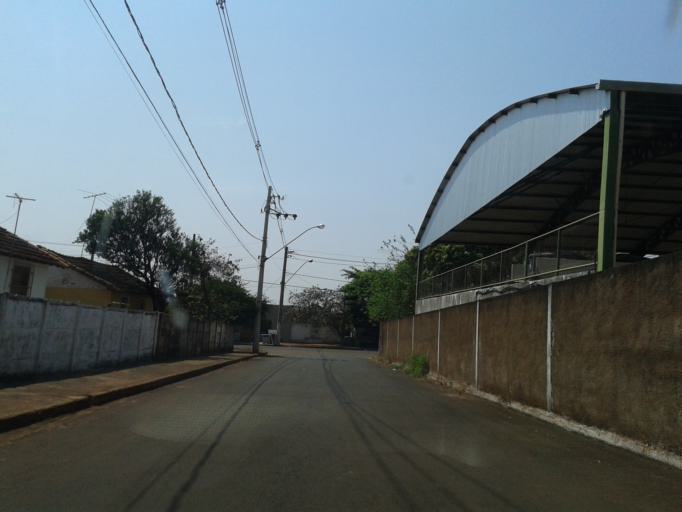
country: BR
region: Minas Gerais
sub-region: Ituiutaba
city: Ituiutaba
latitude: -18.9628
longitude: -49.4509
